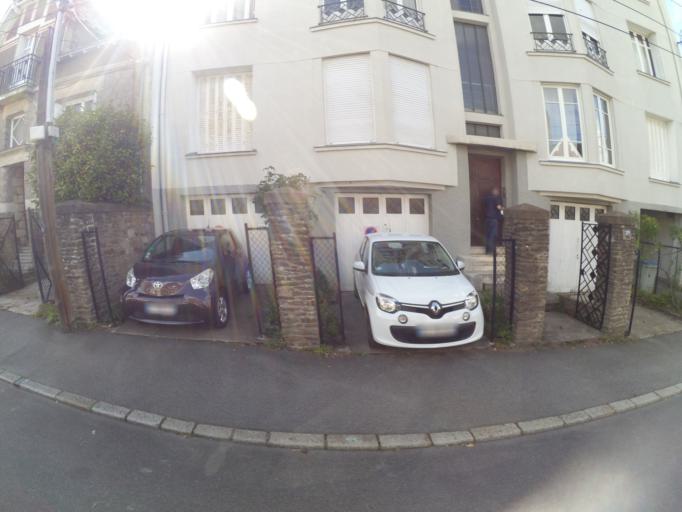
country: FR
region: Pays de la Loire
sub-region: Departement de la Loire-Atlantique
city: Nantes
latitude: 47.2282
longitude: -1.5634
